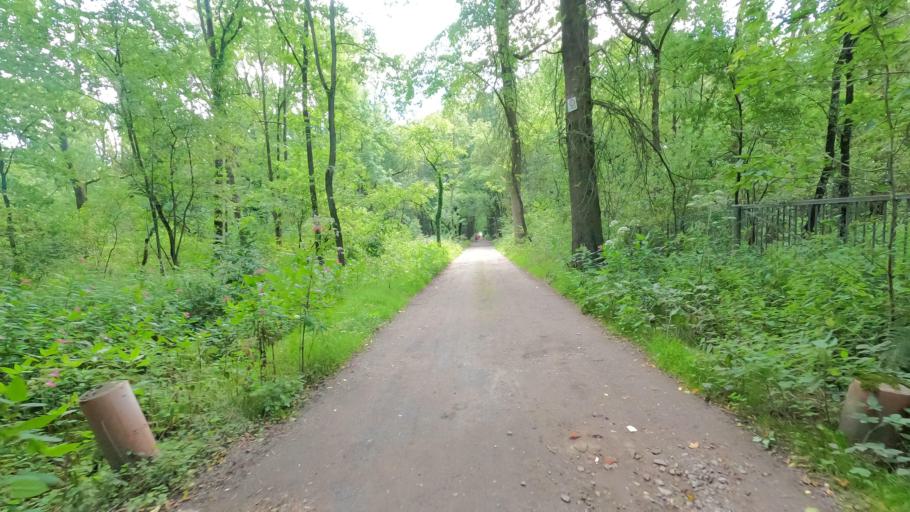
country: BE
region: Flanders
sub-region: Provincie Antwerpen
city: Zoersel
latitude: 51.2500
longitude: 4.7589
